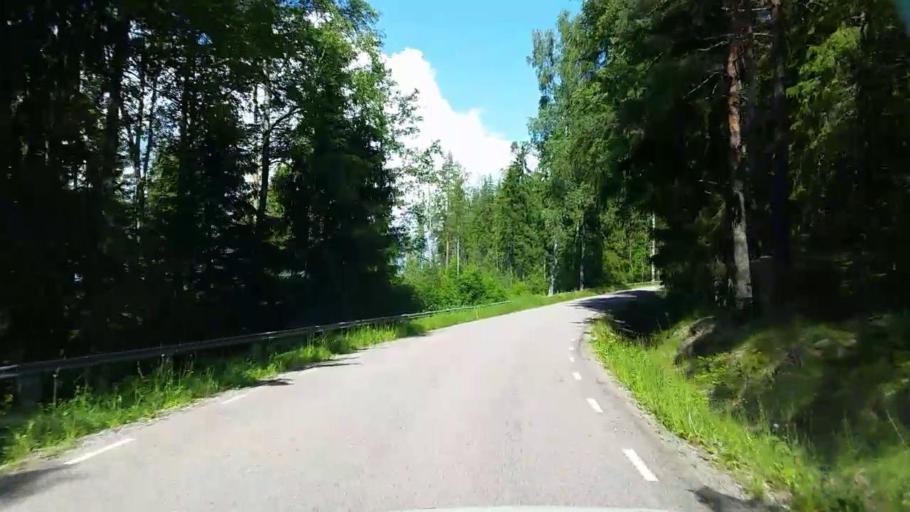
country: SE
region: Vaestmanland
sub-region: Fagersta Kommun
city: Fagersta
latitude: 59.9840
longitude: 15.7406
